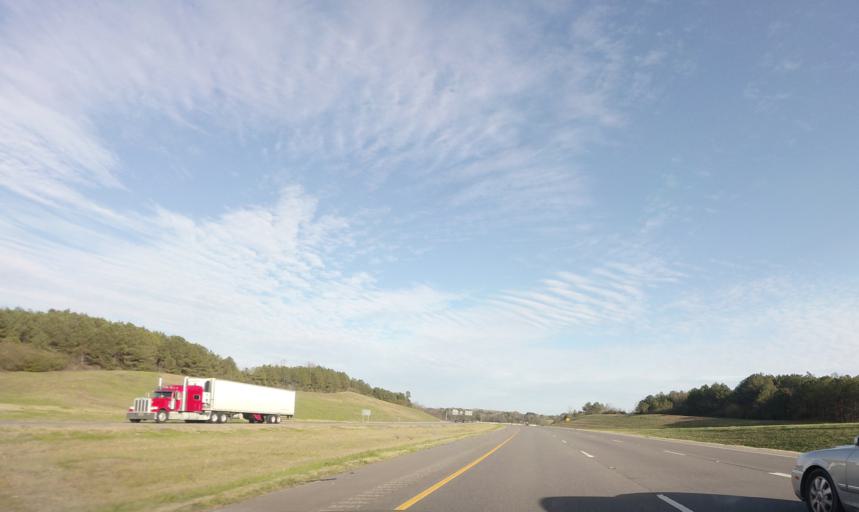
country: US
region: Alabama
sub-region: Walker County
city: Jasper
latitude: 33.8066
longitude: -87.2771
